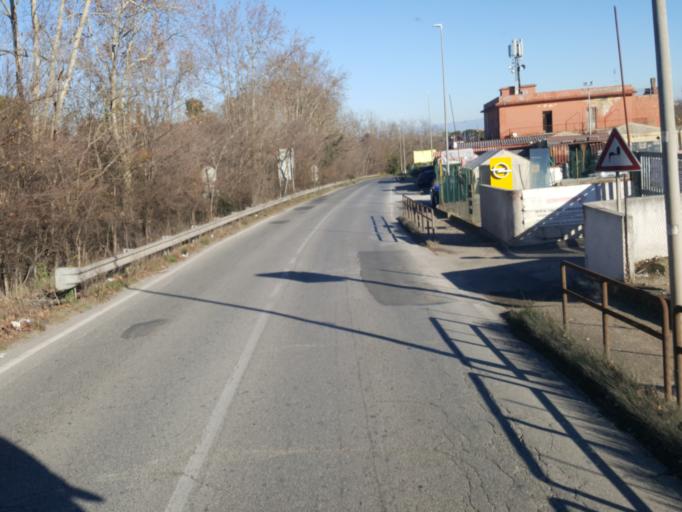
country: IT
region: Latium
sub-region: Citta metropolitana di Roma Capitale
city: Vitinia
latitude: 41.7866
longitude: 12.3688
